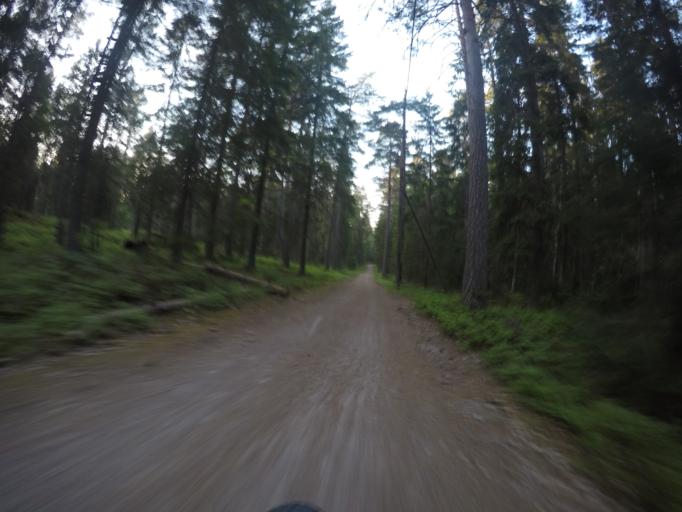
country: SE
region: Soedermanland
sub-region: Eskilstuna Kommun
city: Eskilstuna
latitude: 59.3400
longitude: 16.5107
